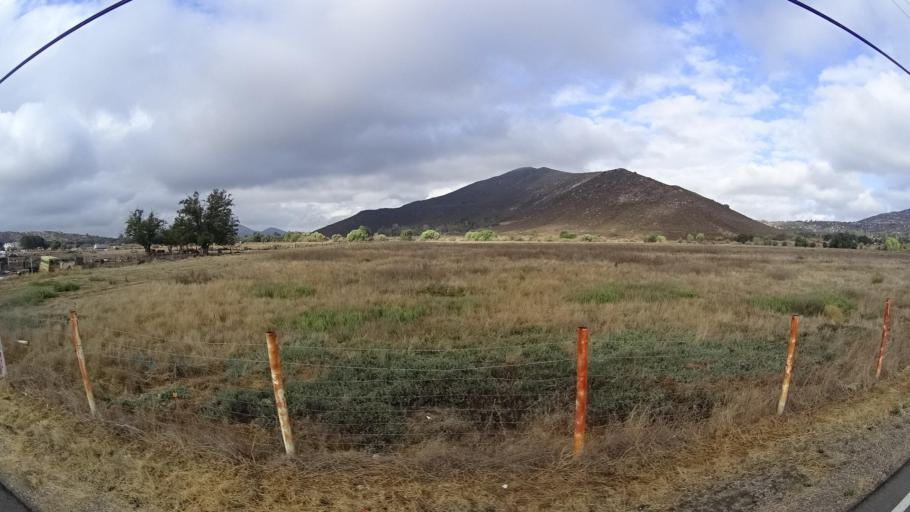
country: MX
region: Baja California
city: Tecate
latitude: 32.6163
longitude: -116.6134
